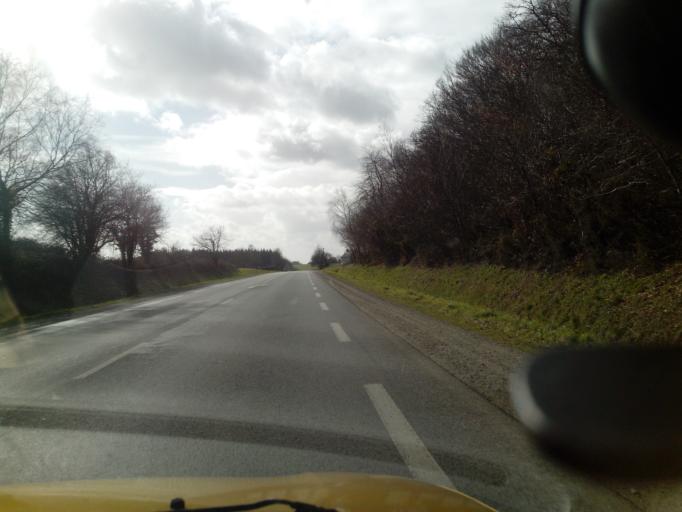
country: FR
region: Brittany
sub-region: Departement du Morbihan
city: Loyat
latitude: 47.9600
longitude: -2.3883
